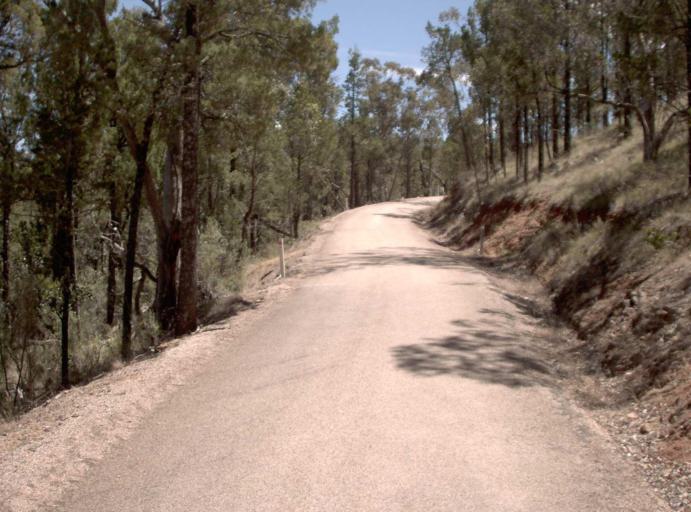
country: AU
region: New South Wales
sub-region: Snowy River
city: Jindabyne
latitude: -36.9489
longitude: 148.3368
